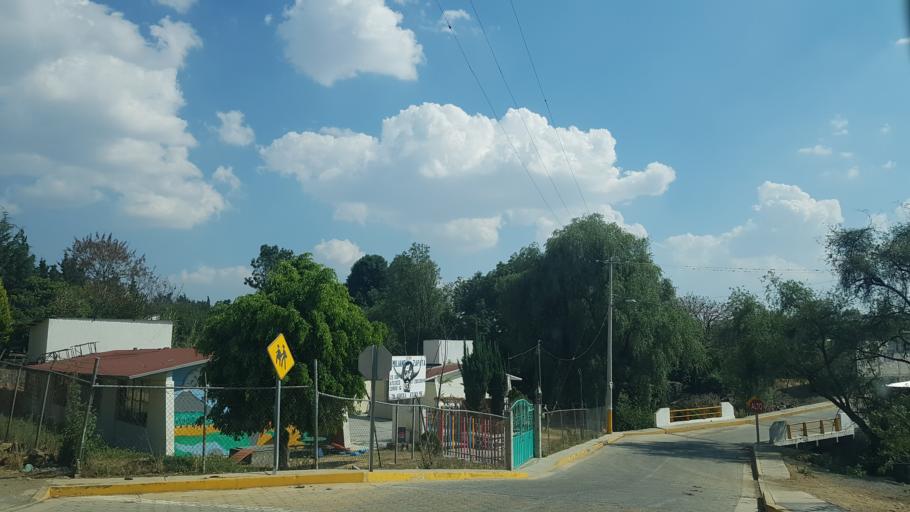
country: MX
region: Puebla
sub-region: Atlixco
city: Colonia Agricola de Ocotepec (Colonia San Jose)
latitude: 18.9251
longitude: -98.5418
